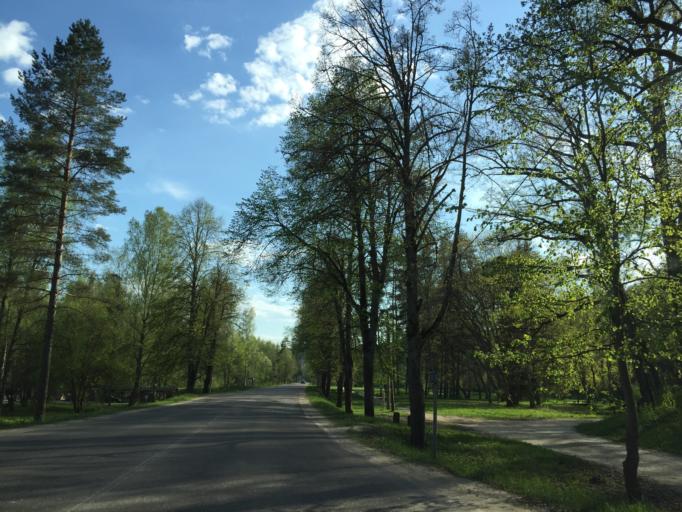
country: LV
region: Sigulda
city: Sigulda
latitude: 57.1770
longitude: 24.8470
